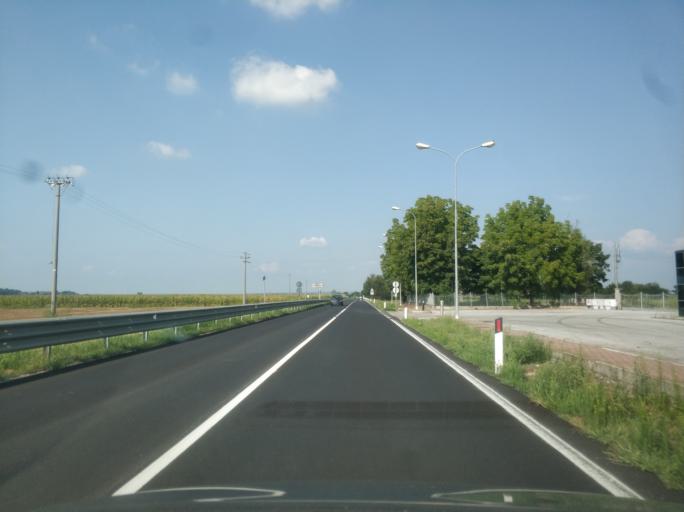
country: IT
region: Piedmont
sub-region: Provincia di Cuneo
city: Cervere
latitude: 44.6079
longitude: 7.7686
